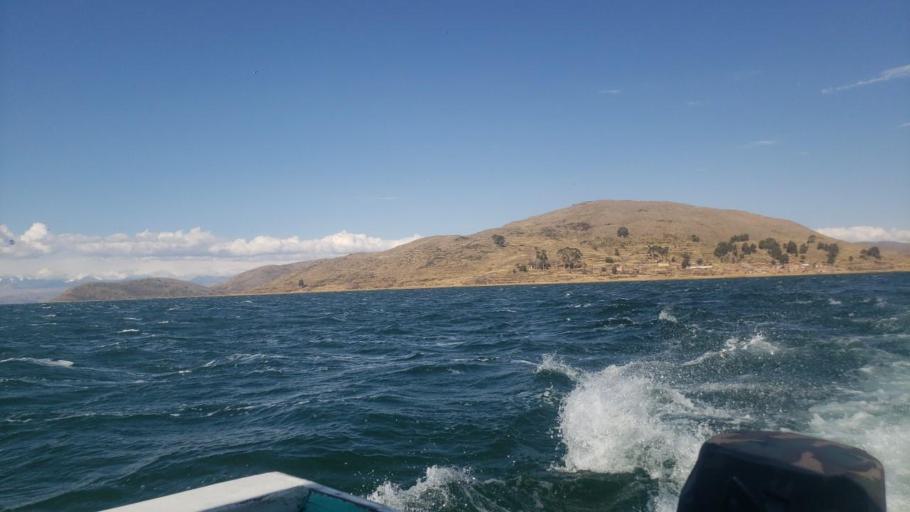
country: BO
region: La Paz
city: Huatajata
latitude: -16.3246
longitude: -68.7271
